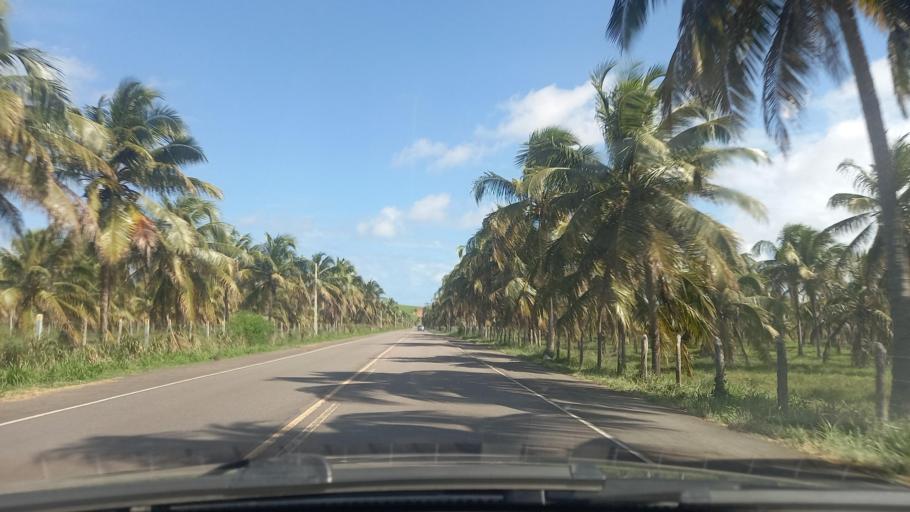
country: BR
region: Alagoas
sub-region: Marechal Deodoro
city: Marechal Deodoro
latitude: -9.8505
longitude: -35.9175
